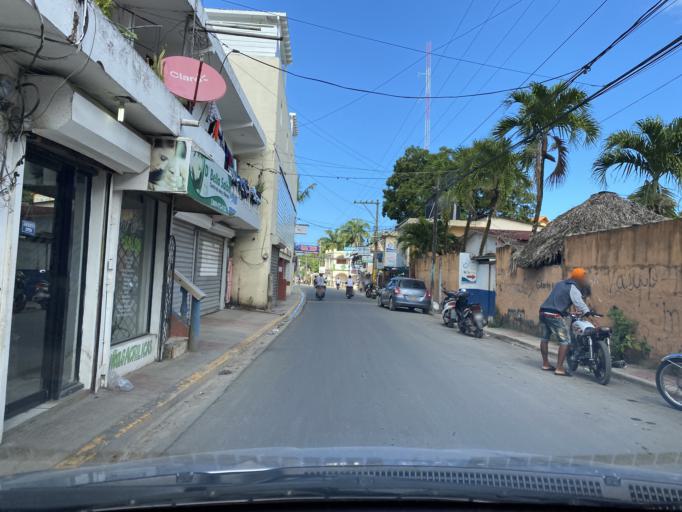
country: DO
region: Samana
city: Las Terrenas
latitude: 19.3097
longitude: -69.5429
